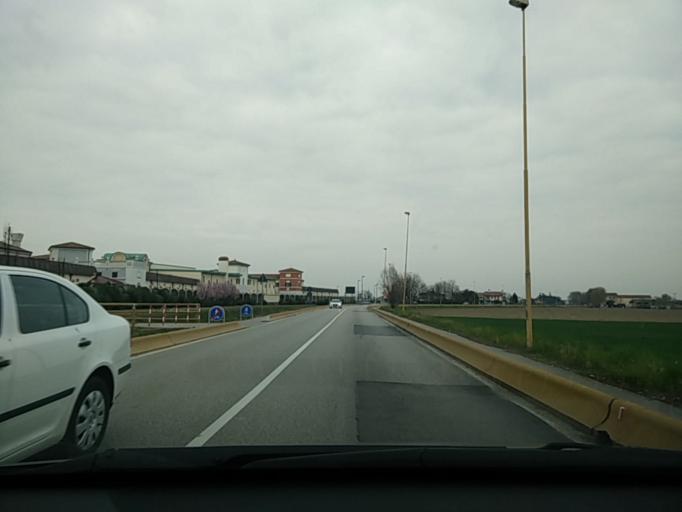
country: IT
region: Veneto
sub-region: Provincia di Venezia
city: Noventa di Piave
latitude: 45.6703
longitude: 12.5373
